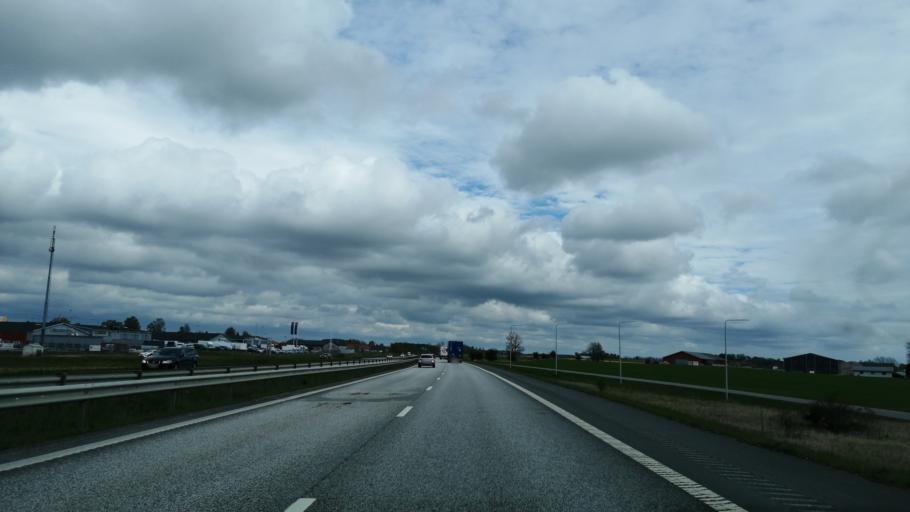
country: SE
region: Skane
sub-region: Kristianstads Kommun
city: Kristianstad
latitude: 56.0252
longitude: 14.2116
